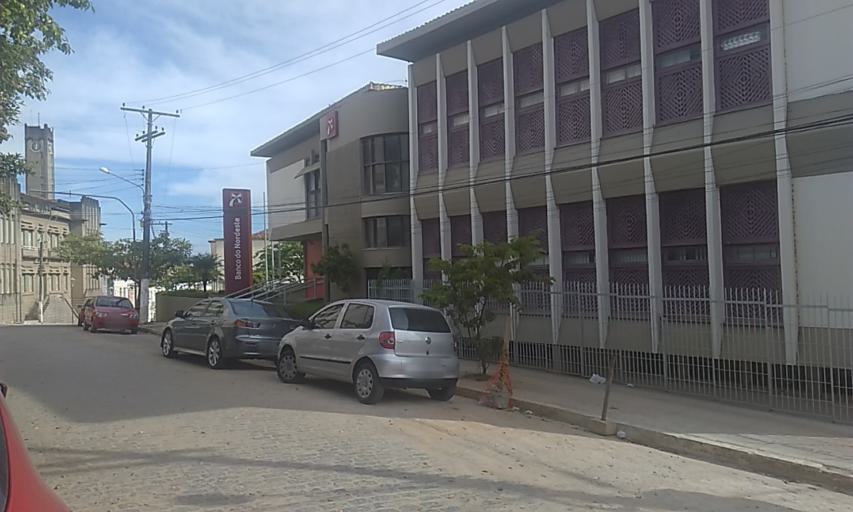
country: BR
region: Alagoas
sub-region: Penedo
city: Penedo
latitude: -10.2901
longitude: -36.5860
